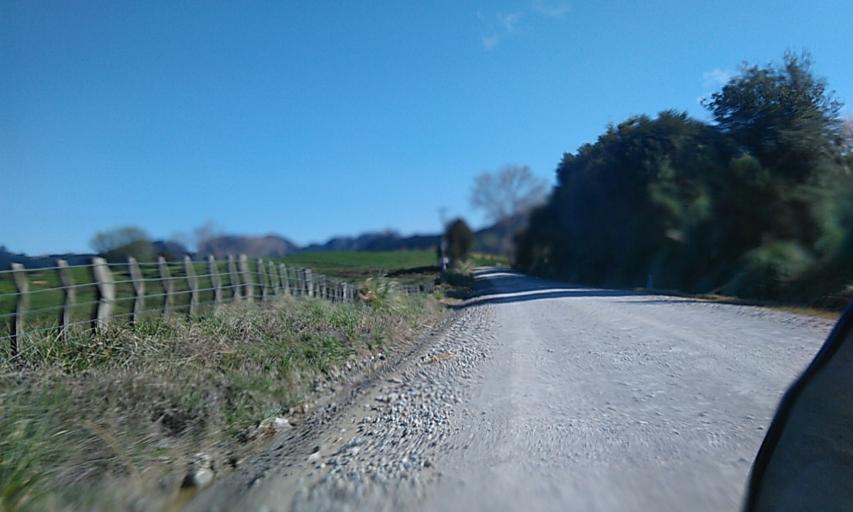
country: NZ
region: Gisborne
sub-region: Gisborne District
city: Gisborne
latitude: -38.4931
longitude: 178.0590
